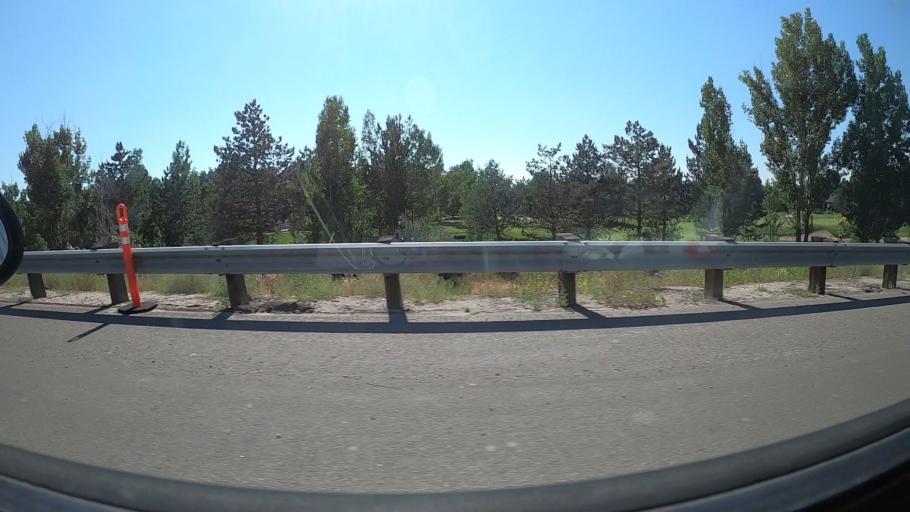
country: US
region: Idaho
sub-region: Ada County
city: Eagle
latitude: 43.6676
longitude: -116.3545
